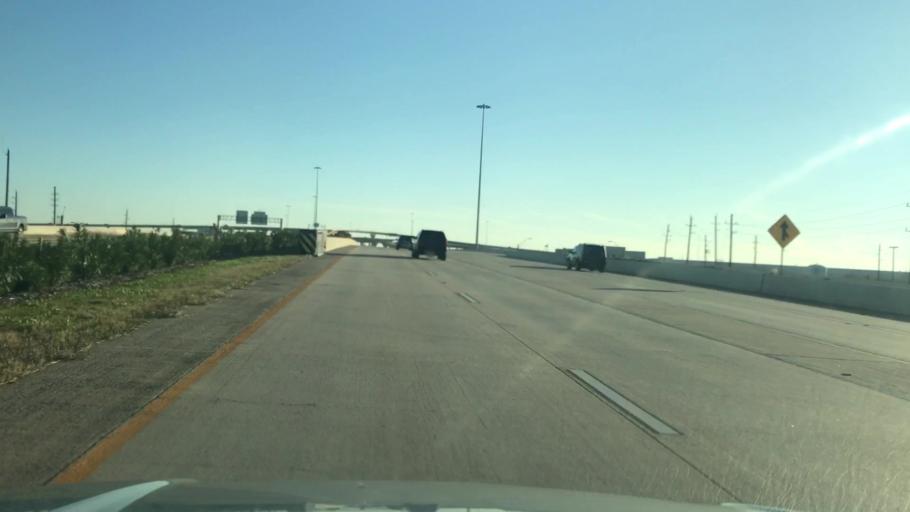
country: US
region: Texas
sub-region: Harris County
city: Katy
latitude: 29.7953
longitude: -95.7764
